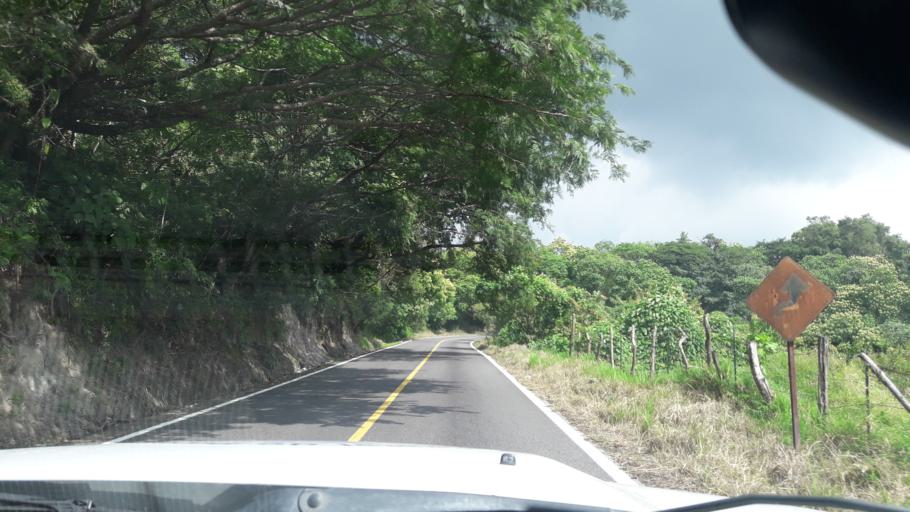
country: MX
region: Colima
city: Suchitlan
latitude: 19.4355
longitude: -103.7053
